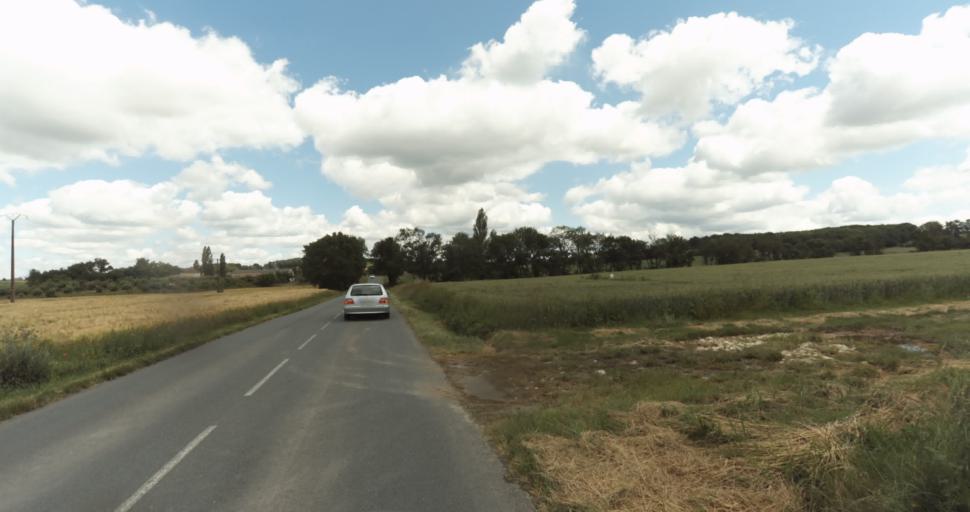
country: FR
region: Aquitaine
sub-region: Departement de la Dordogne
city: Beaumont-du-Perigord
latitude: 44.7196
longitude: 0.7539
